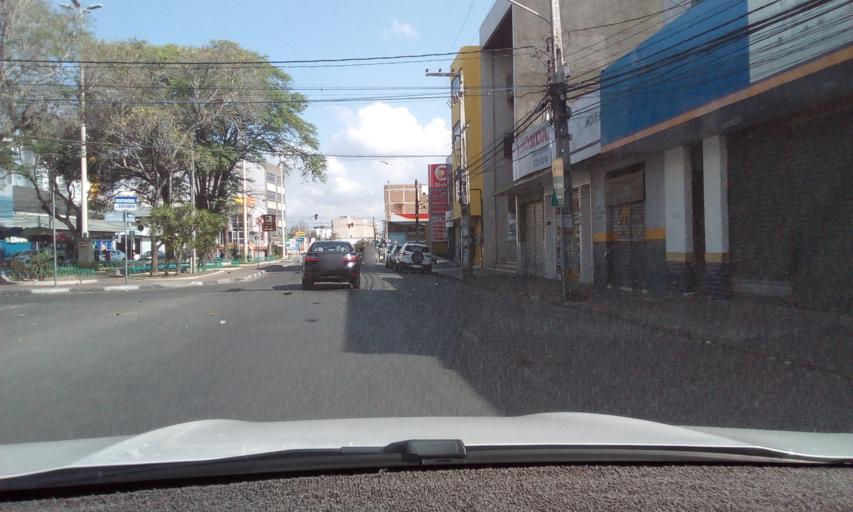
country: BR
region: Pernambuco
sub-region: Caruaru
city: Caruaru
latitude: -8.2795
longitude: -35.9736
